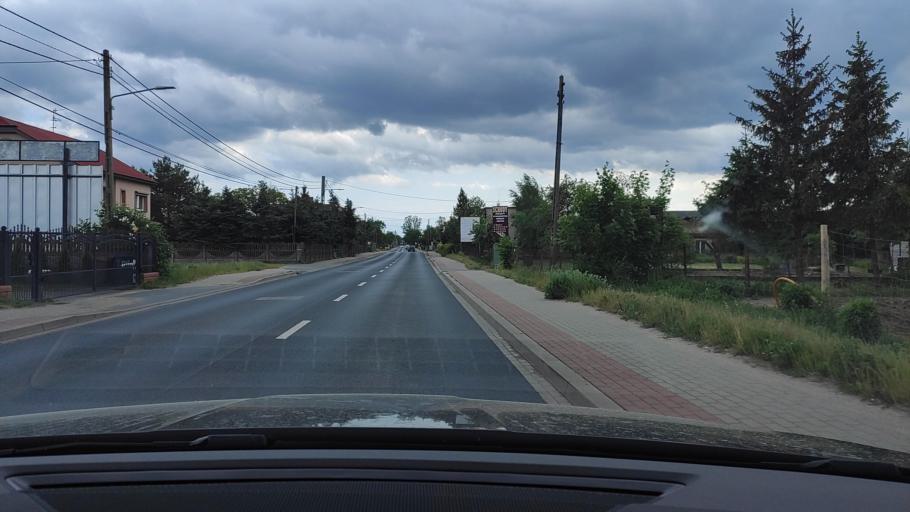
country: PL
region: Greater Poland Voivodeship
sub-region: Powiat poznanski
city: Swarzedz
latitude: 52.3936
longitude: 17.0765
